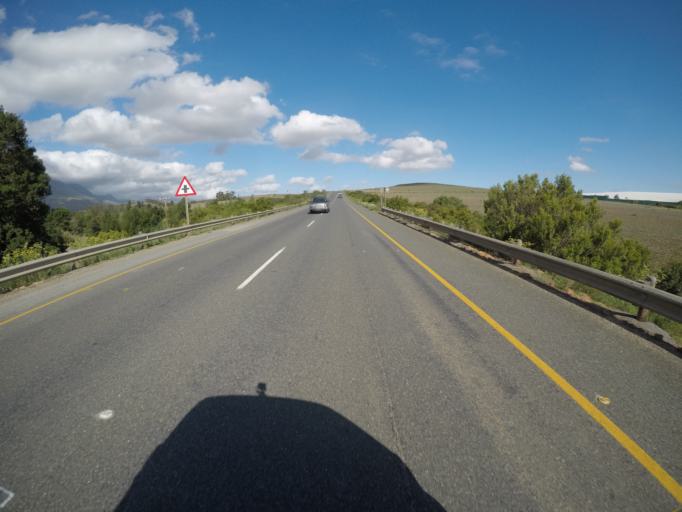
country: ZA
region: Western Cape
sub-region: Overberg District Municipality
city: Swellendam
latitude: -33.9649
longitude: 20.2457
